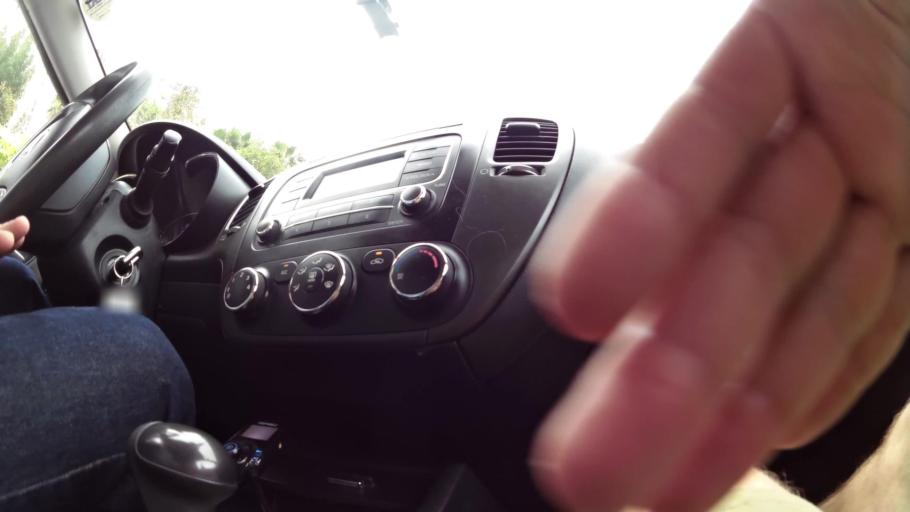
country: BH
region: Manama
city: Manama
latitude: 26.2395
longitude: 50.5841
